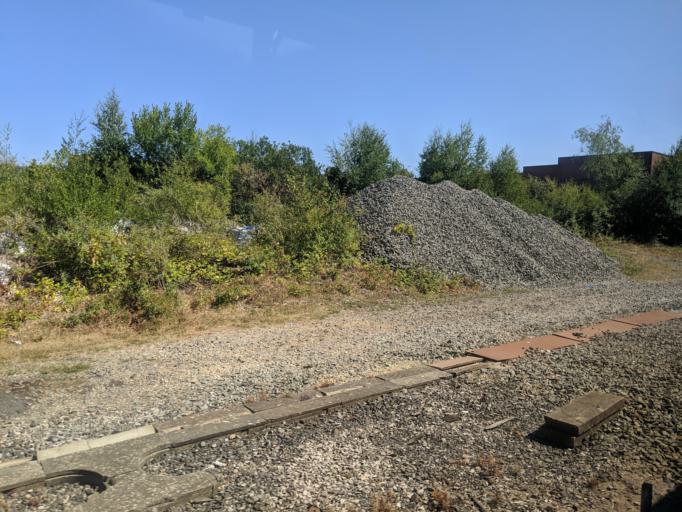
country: GB
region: England
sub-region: Devon
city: Newton Abbot
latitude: 50.5280
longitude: -3.5990
